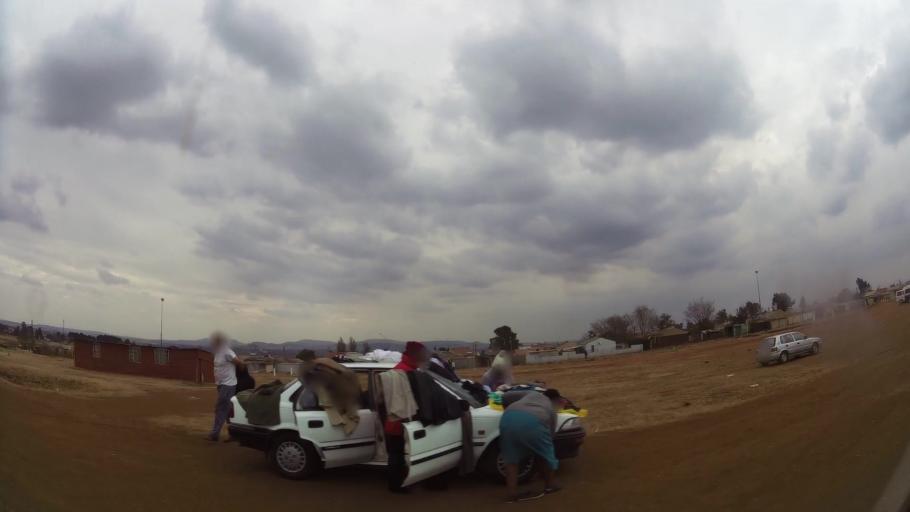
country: ZA
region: Gauteng
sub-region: Ekurhuleni Metropolitan Municipality
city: Germiston
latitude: -26.3979
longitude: 28.1326
